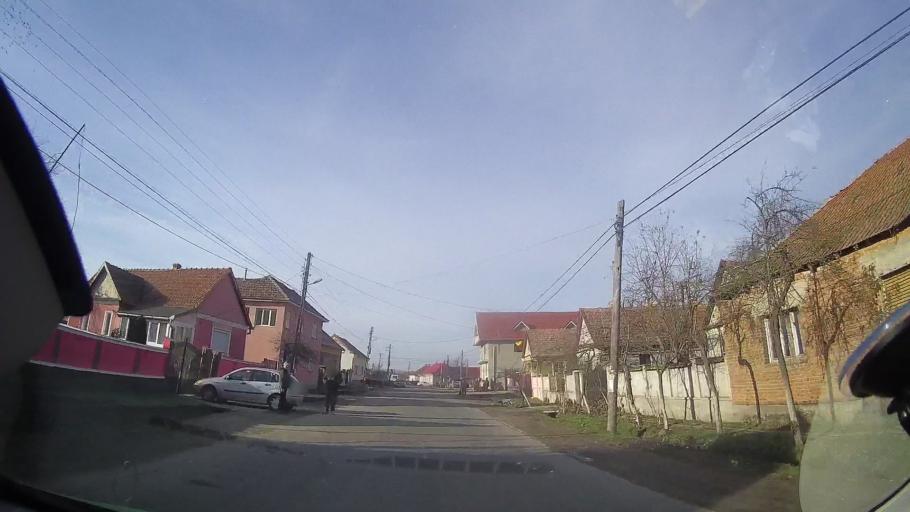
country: RO
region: Bihor
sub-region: Comuna Brusturi
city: Brusturi
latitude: 47.1567
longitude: 22.2401
